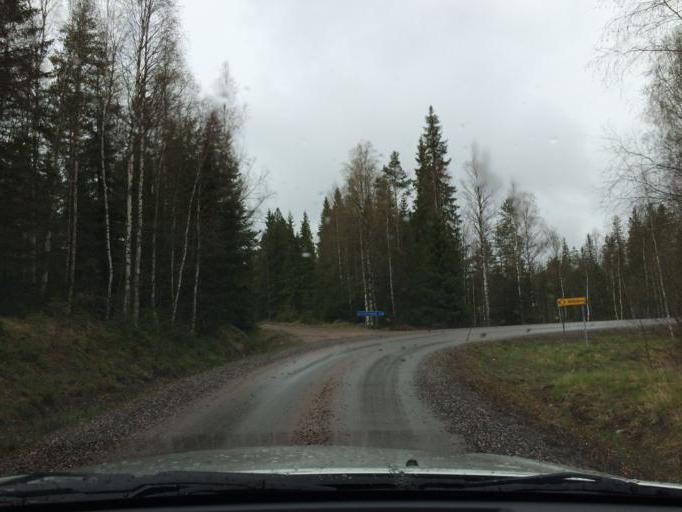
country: SE
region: Dalarna
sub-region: Ludvika Kommun
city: Abborrberget
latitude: 60.0397
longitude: 14.6392
